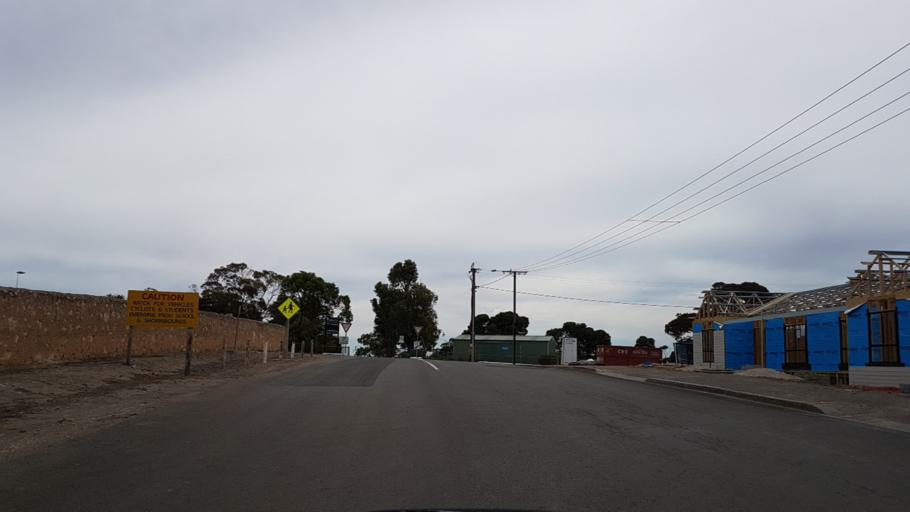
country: AU
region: South Australia
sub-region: Yorke Peninsula
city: Port Victoria
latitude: -34.7676
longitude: 137.5938
